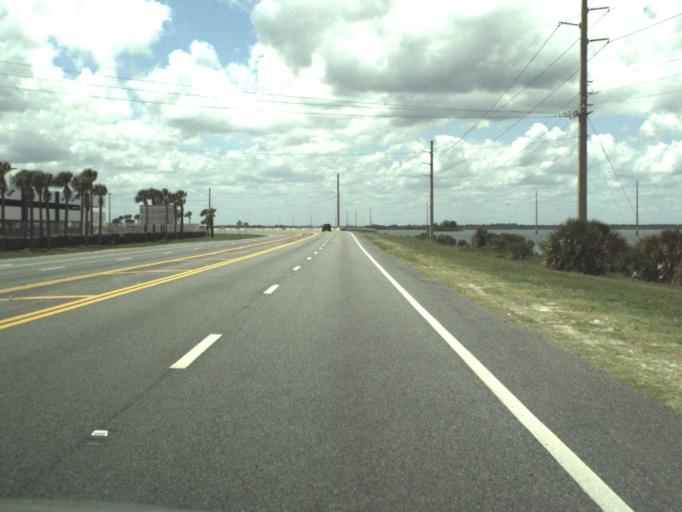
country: US
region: Florida
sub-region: Brevard County
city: Cape Canaveral
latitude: 28.4188
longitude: -80.6270
